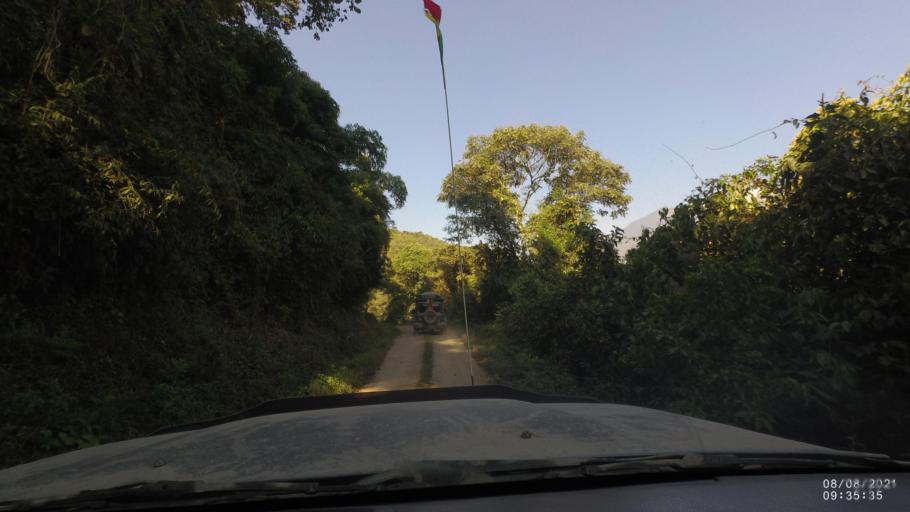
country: BO
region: La Paz
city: Quime
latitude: -16.5922
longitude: -66.7055
